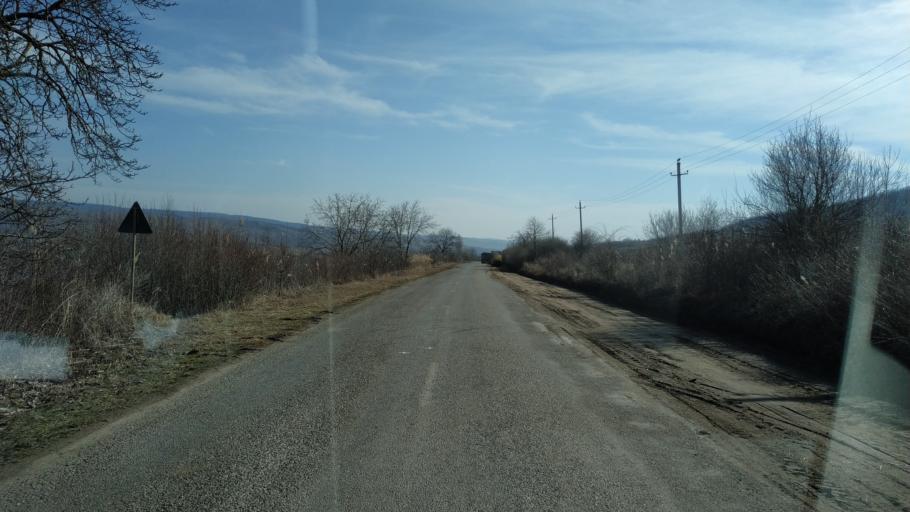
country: MD
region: Nisporeni
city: Nisporeni
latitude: 47.1836
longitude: 28.0756
